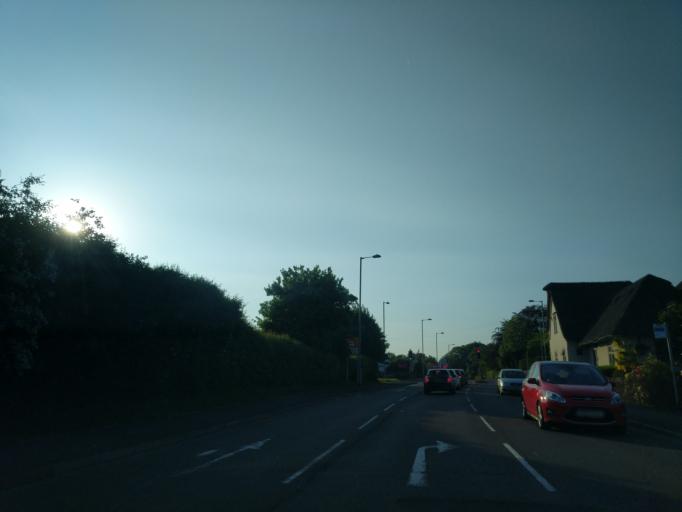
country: GB
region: England
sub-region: Staffordshire
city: Stone
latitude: 52.8906
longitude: -2.1259
